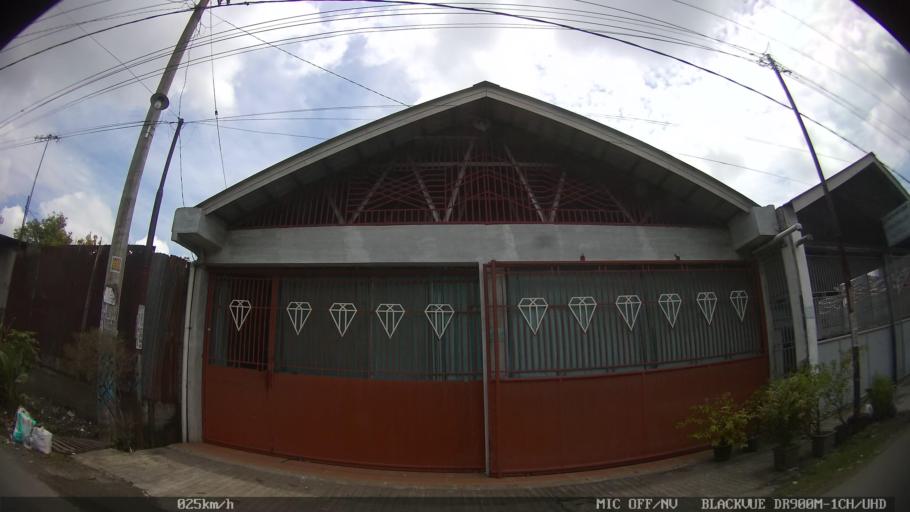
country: ID
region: North Sumatra
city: Medan
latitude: 3.6083
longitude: 98.7489
